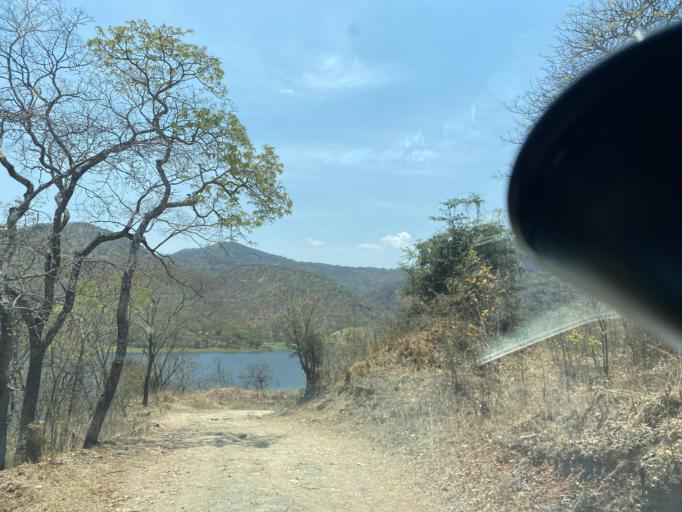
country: ZM
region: Lusaka
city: Kafue
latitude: -15.8049
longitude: 28.4239
